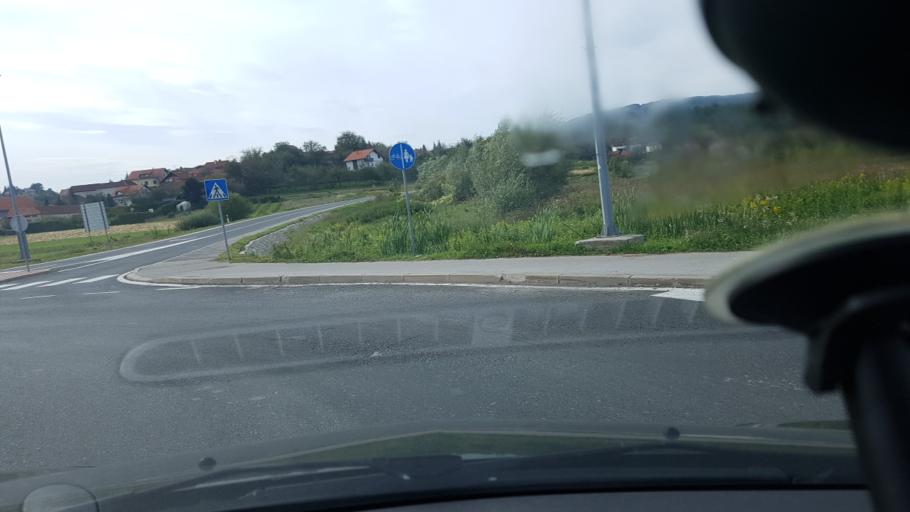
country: HR
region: Varazdinska
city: Remetinec
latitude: 46.1566
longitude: 16.3341
